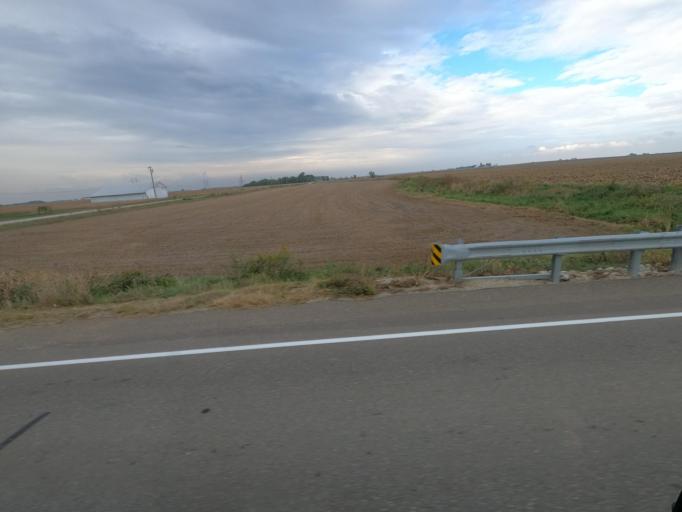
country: US
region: Iowa
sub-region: Henry County
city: Mount Pleasant
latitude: 40.7846
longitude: -91.6406
